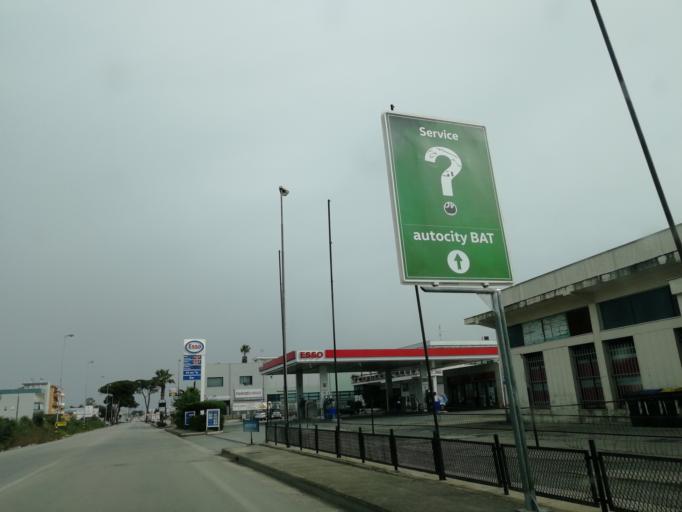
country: IT
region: Apulia
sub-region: Provincia di Barletta - Andria - Trani
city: Barletta
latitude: 41.3100
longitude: 16.3099
